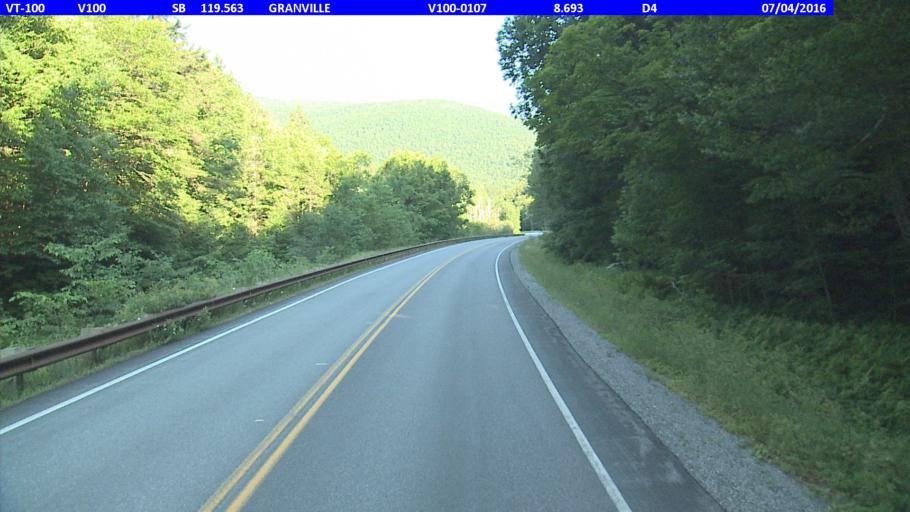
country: US
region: Vermont
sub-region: Washington County
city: Northfield
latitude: 44.0541
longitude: -72.8352
